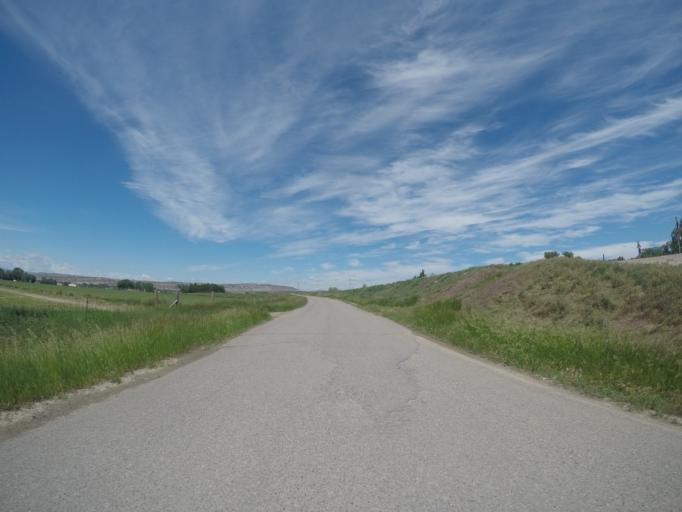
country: US
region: Montana
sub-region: Carbon County
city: Red Lodge
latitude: 45.2561
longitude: -108.8867
